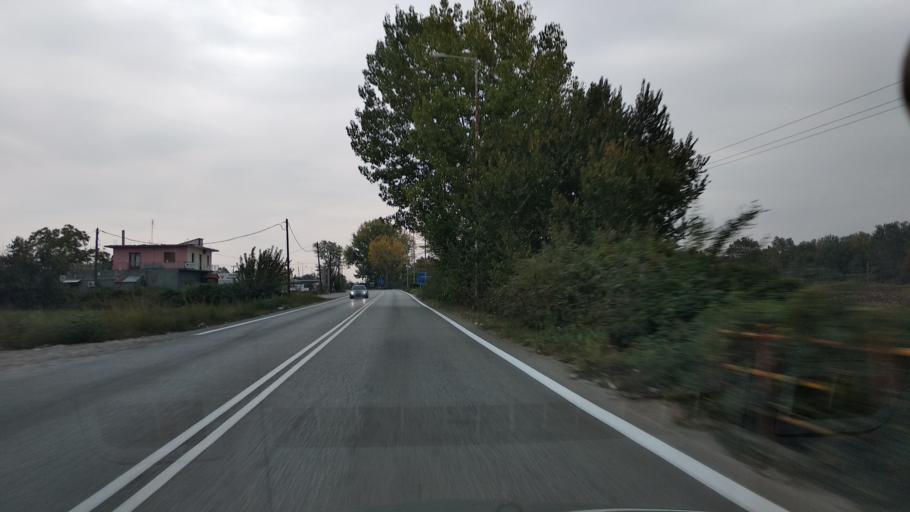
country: GR
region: Thessaly
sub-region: Trikala
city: Pyrgetos
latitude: 39.5285
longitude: 21.7406
